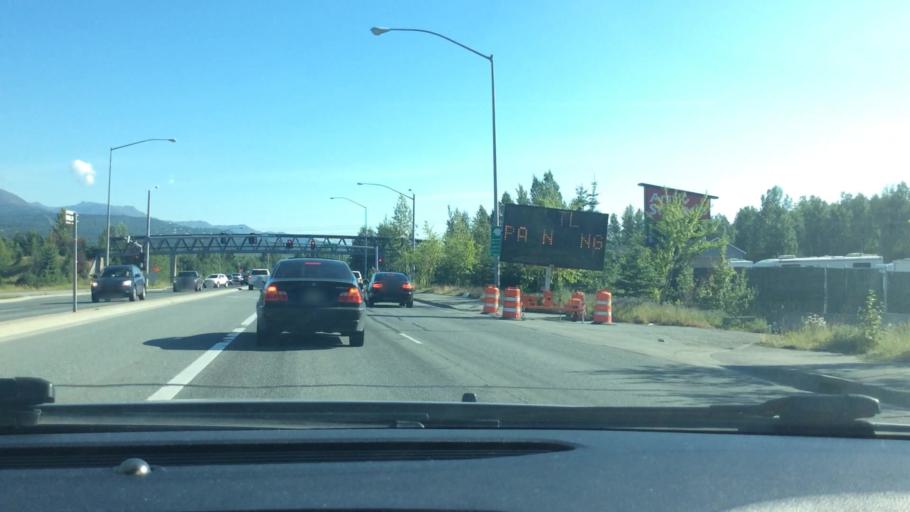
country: US
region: Alaska
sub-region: Anchorage Municipality
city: Elmendorf Air Force Base
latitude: 61.1893
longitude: -149.7333
